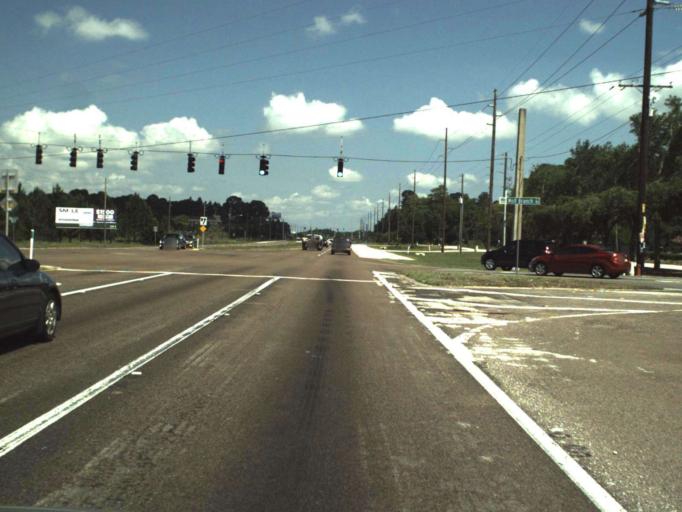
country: US
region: Florida
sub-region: Lake County
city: Mount Dora
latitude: 28.8149
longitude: -81.6283
